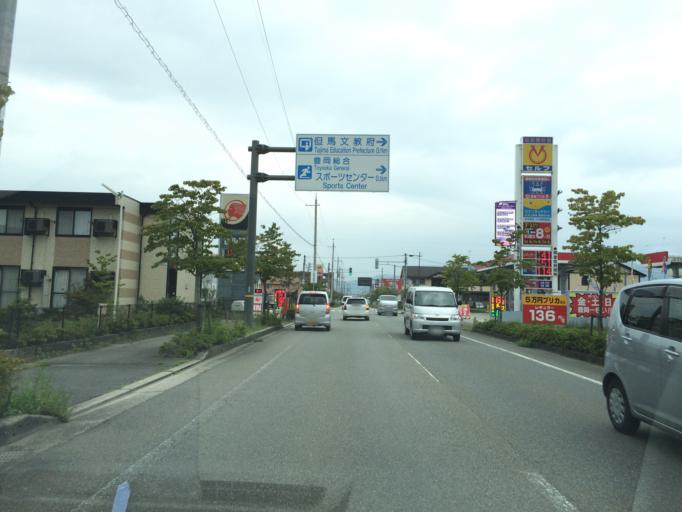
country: JP
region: Hyogo
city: Toyooka
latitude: 35.5342
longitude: 134.8083
